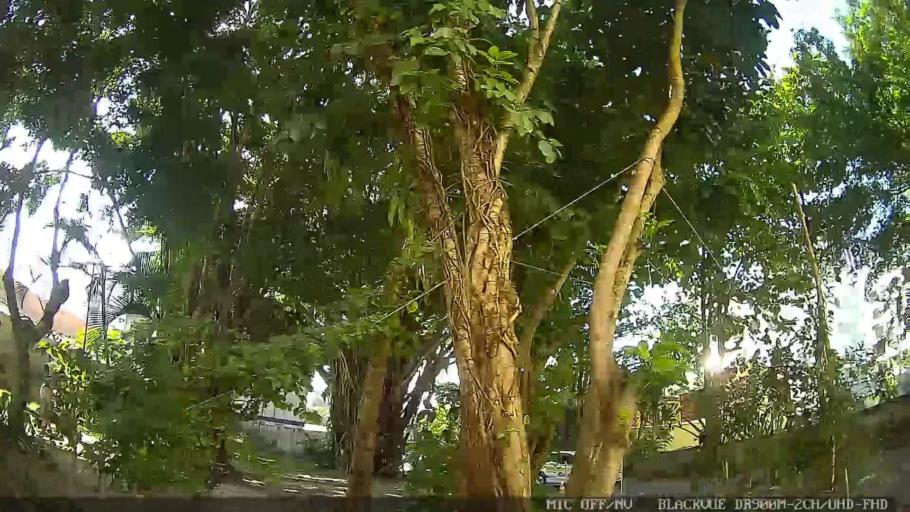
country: BR
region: Sao Paulo
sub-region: Guaruja
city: Guaruja
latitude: -24.0125
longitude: -46.2757
